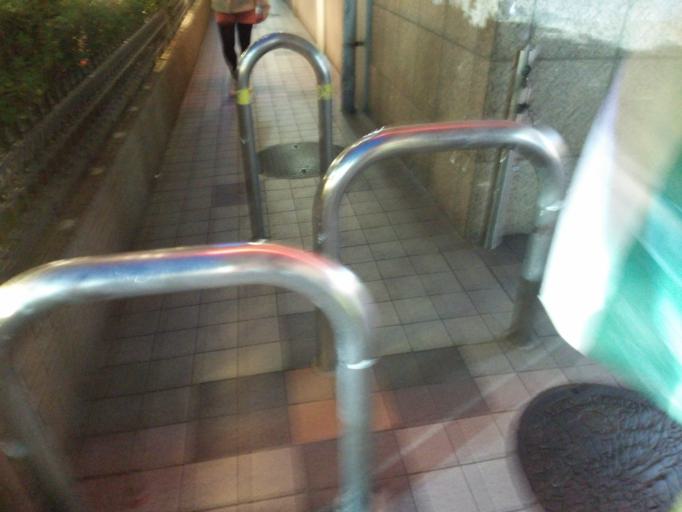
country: JP
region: Osaka
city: Takatsuki
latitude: 34.8490
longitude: 135.6218
